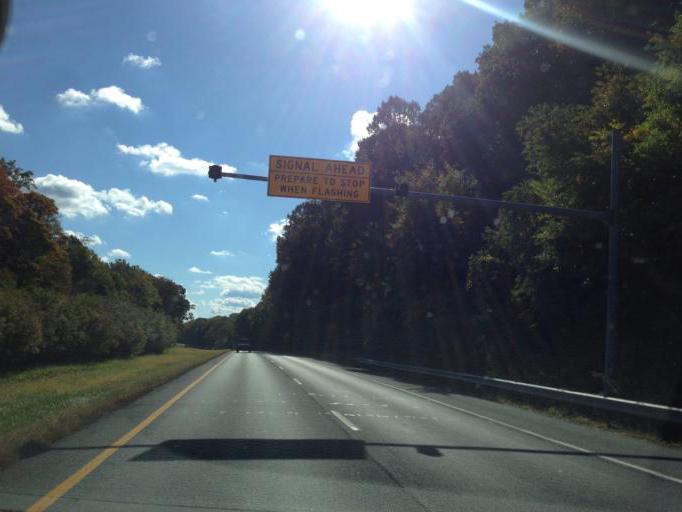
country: US
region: Maryland
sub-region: Howard County
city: Columbia
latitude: 39.2983
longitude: -76.9060
